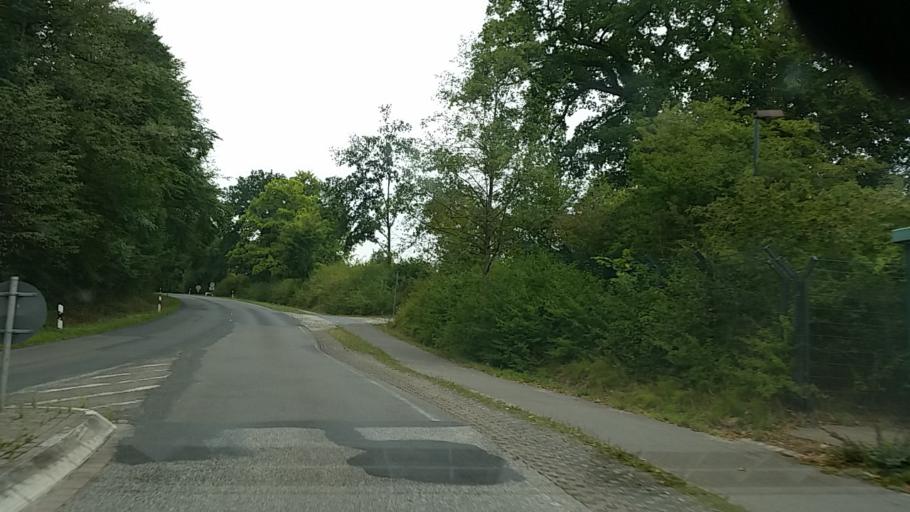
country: DE
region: Schleswig-Holstein
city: Aumuhle
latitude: 53.5312
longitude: 10.3066
